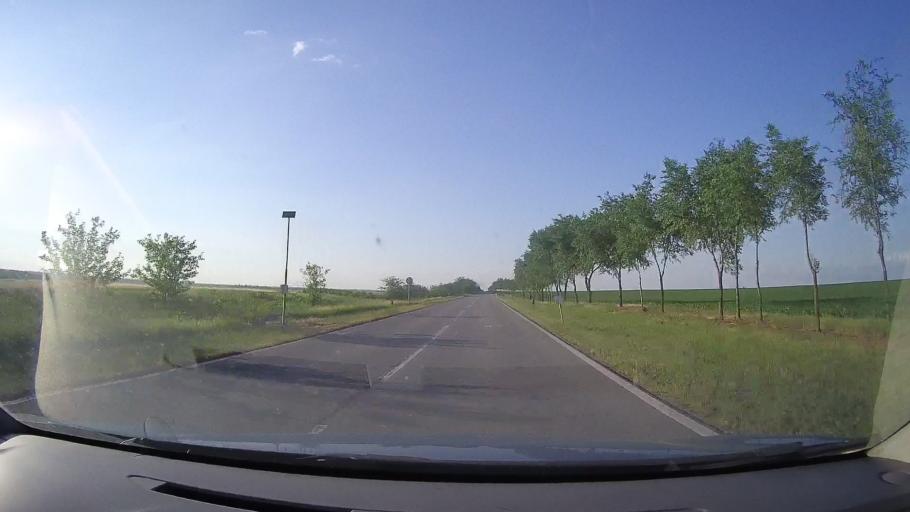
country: RO
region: Timis
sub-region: Comuna Moravita
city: Moravita
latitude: 45.1990
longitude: 21.2999
